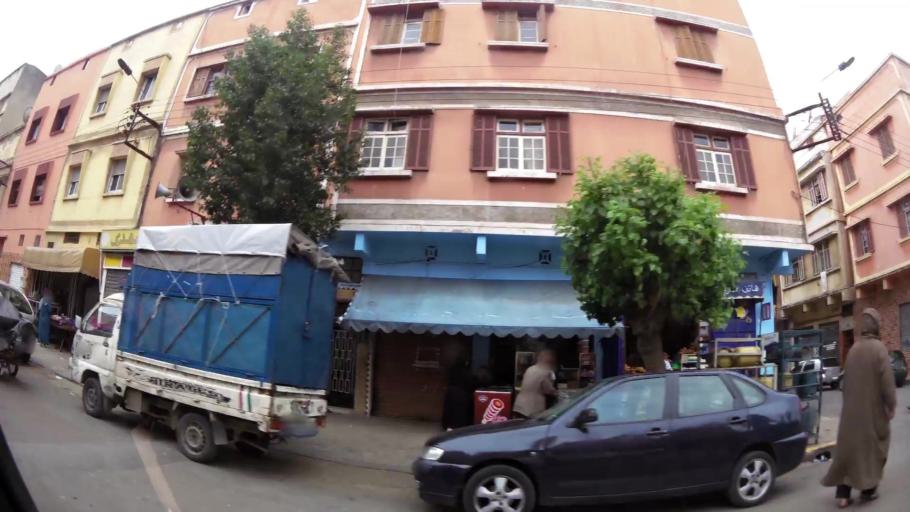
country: MA
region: Grand Casablanca
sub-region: Casablanca
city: Casablanca
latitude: 33.5670
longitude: -7.5682
